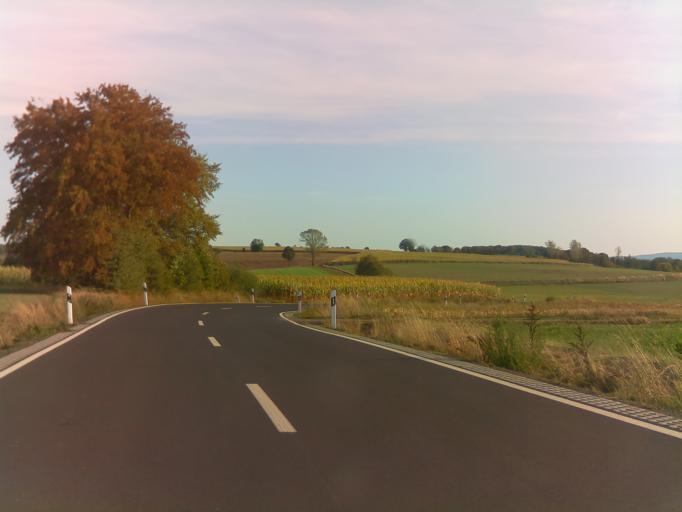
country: DE
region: Hesse
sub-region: Regierungsbezirk Giessen
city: Freiensteinau
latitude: 50.3828
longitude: 9.4291
